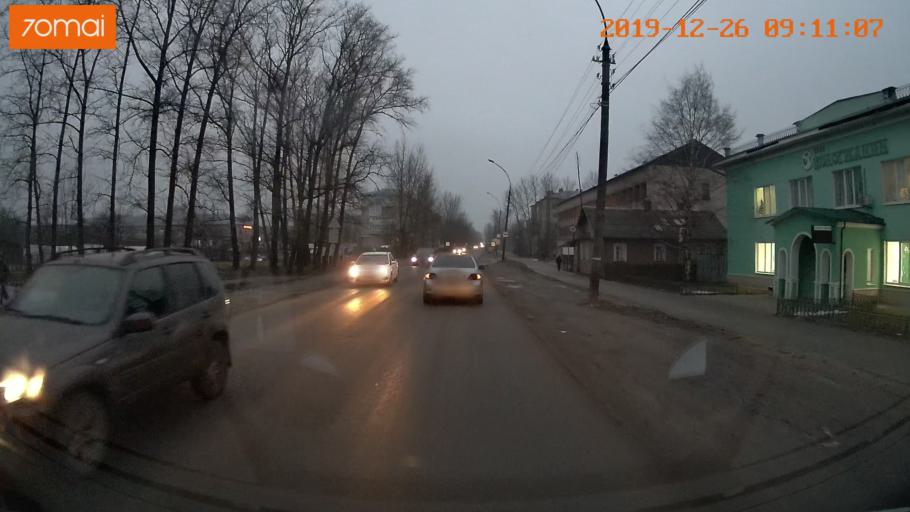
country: RU
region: Vologda
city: Gryazovets
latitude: 58.8744
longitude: 40.2525
